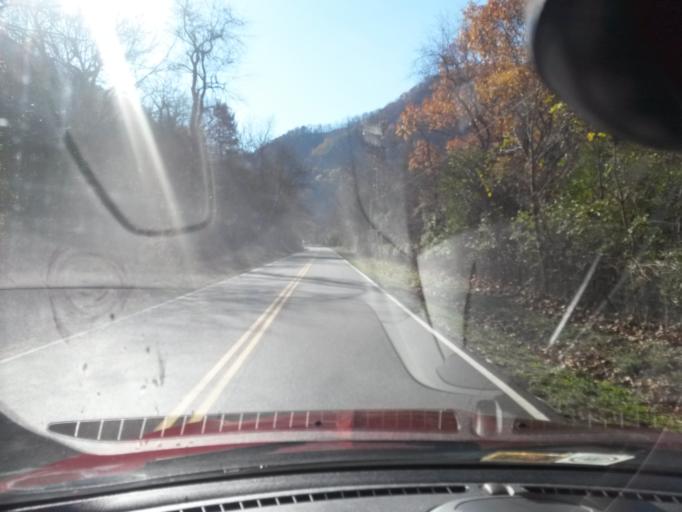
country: US
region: Virginia
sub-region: Botetourt County
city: Fincastle
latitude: 37.6493
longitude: -79.8084
